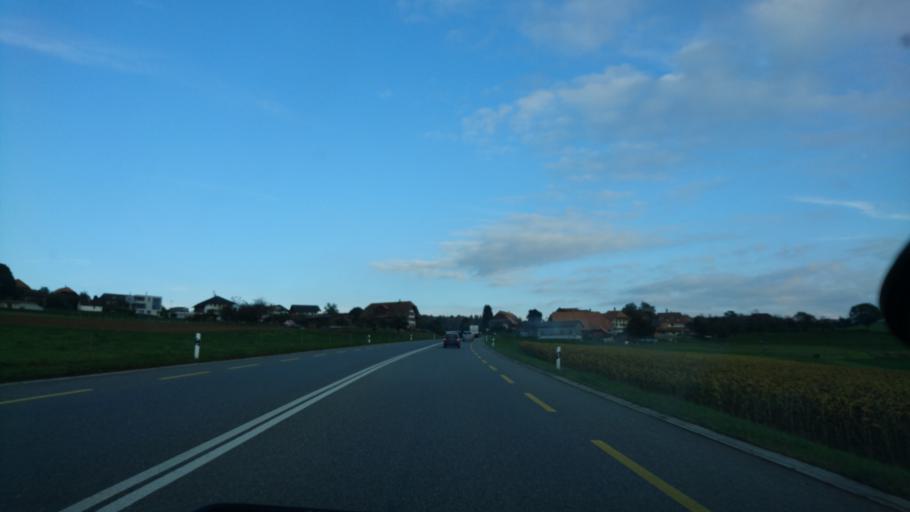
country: CH
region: Bern
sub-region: Bern-Mittelland District
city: Biglen
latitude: 46.9179
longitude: 7.6081
